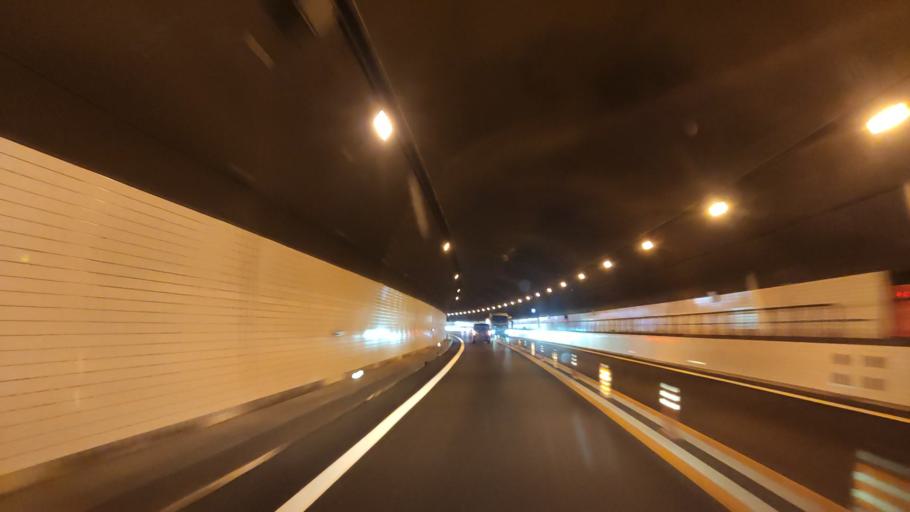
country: JP
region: Tokushima
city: Ikedacho
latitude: 34.0509
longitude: 133.9193
